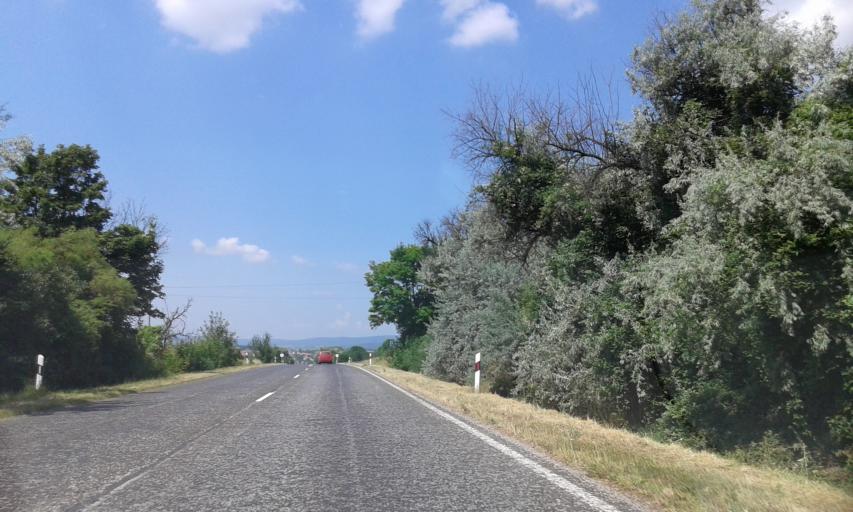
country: HU
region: Fejer
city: Bicske
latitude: 47.4949
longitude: 18.6642
